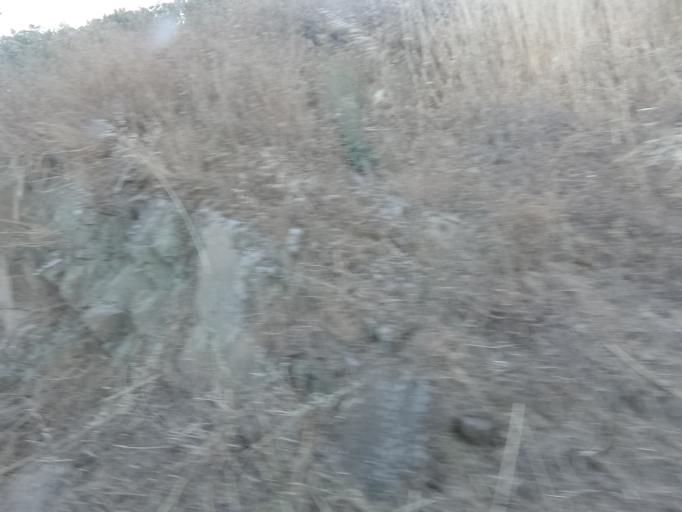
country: PT
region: Vila Real
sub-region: Sabrosa
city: Vilela
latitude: 41.1810
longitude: -7.5882
